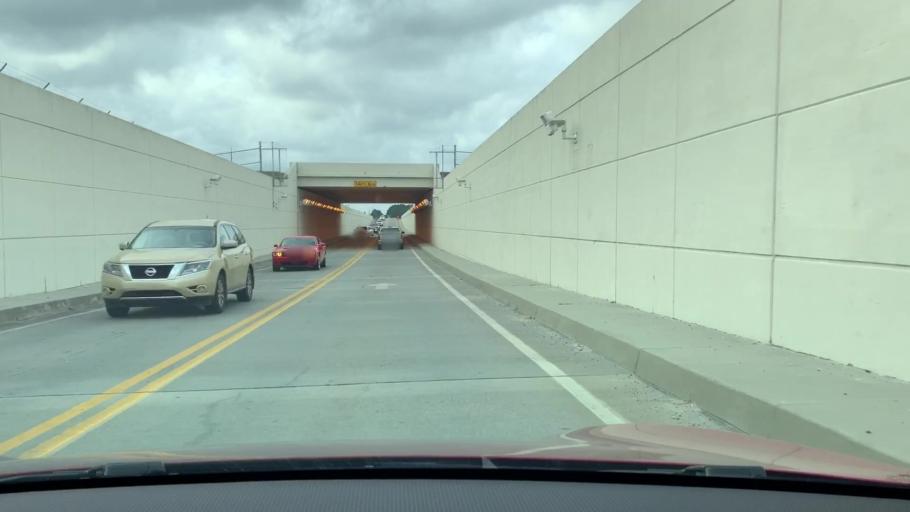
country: US
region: Georgia
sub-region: Chatham County
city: Port Wentworth
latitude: 32.1421
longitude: -81.2024
